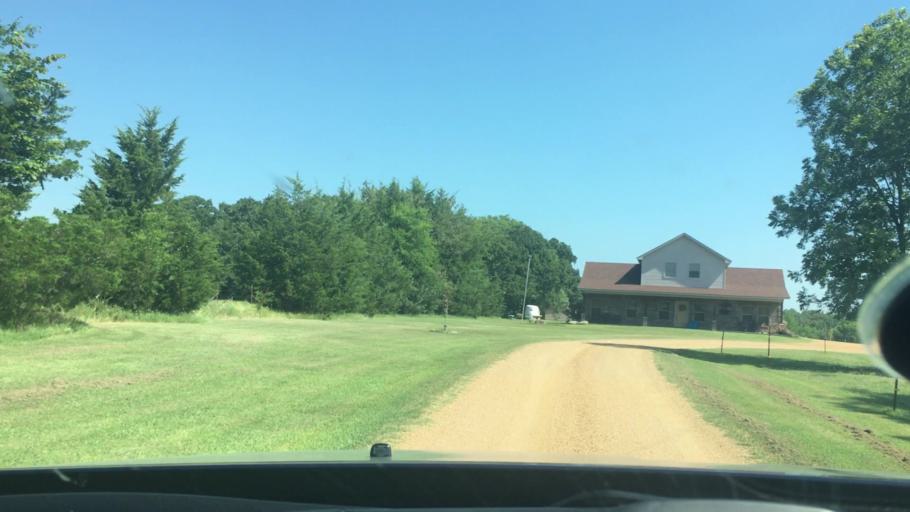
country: US
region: Oklahoma
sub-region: Johnston County
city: Tishomingo
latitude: 34.3108
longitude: -96.6100
